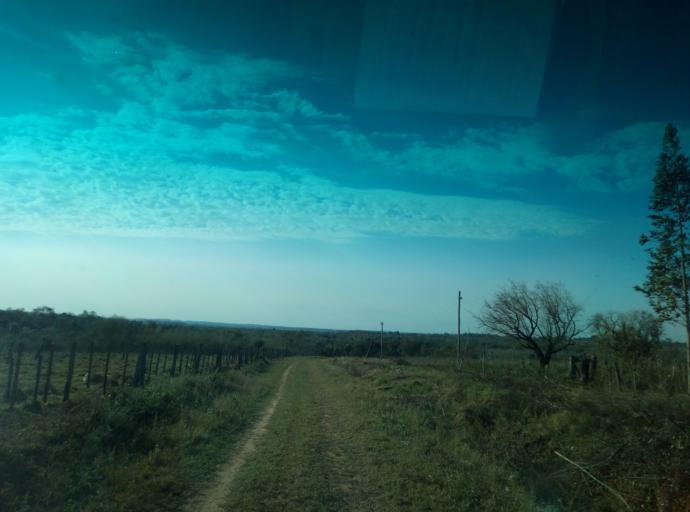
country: PY
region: Caaguazu
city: Doctor Cecilio Baez
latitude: -25.1603
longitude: -56.2320
